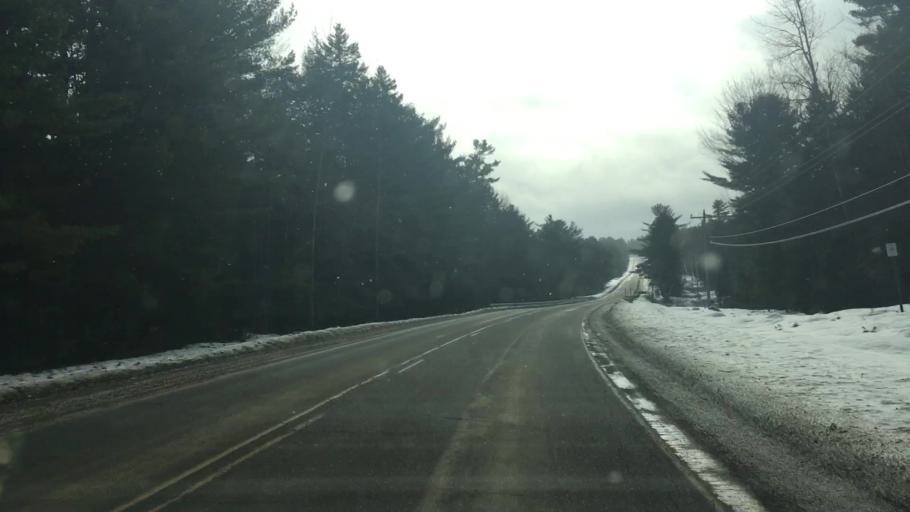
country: US
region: Maine
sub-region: Washington County
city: Calais
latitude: 45.0754
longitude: -67.3324
